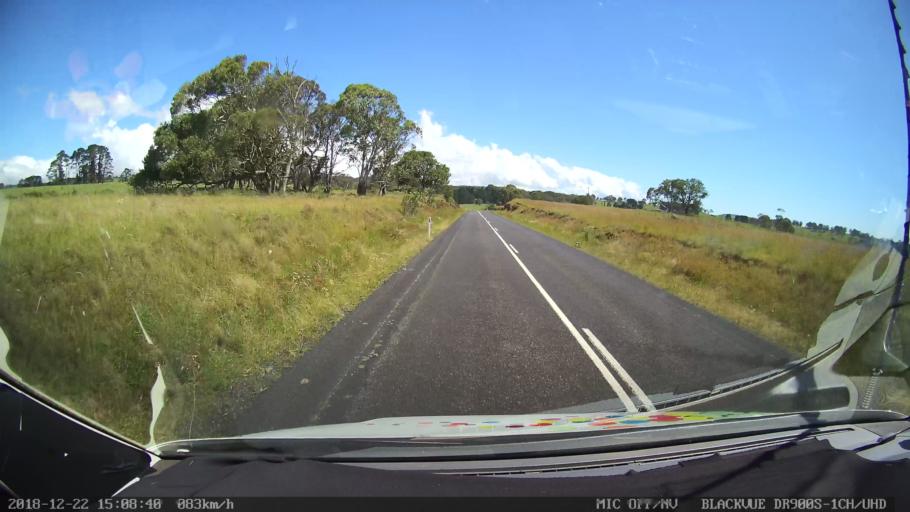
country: AU
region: New South Wales
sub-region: Bellingen
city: Dorrigo
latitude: -30.3153
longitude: 152.4129
